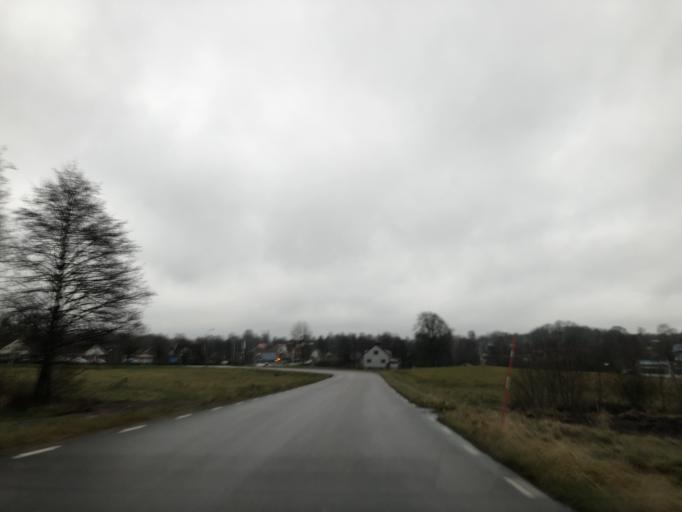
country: SE
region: Vaestra Goetaland
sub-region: Ulricehamns Kommun
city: Ulricehamn
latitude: 57.8427
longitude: 13.2793
